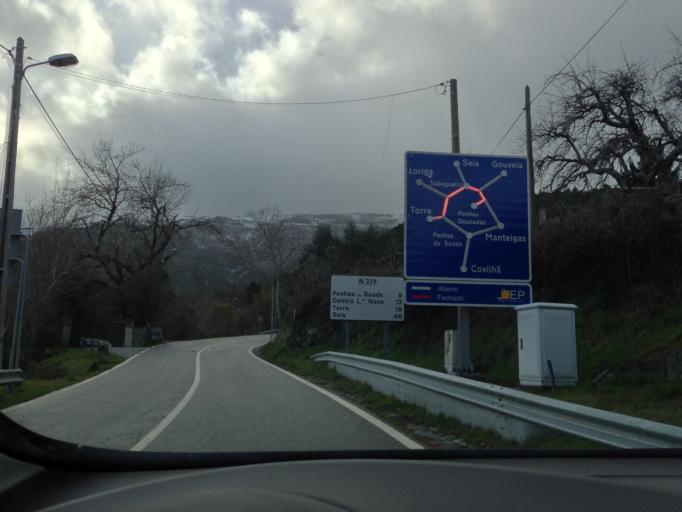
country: PT
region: Castelo Branco
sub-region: Covilha
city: Covilha
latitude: 40.2813
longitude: -7.5148
